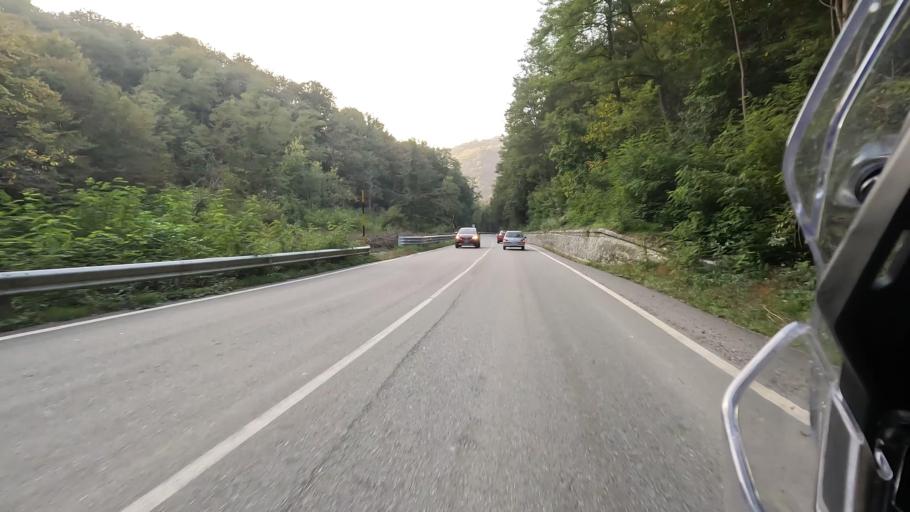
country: IT
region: Liguria
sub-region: Provincia di Savona
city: Osteria dei Cacciatori-Stella
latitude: 44.4456
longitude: 8.4818
